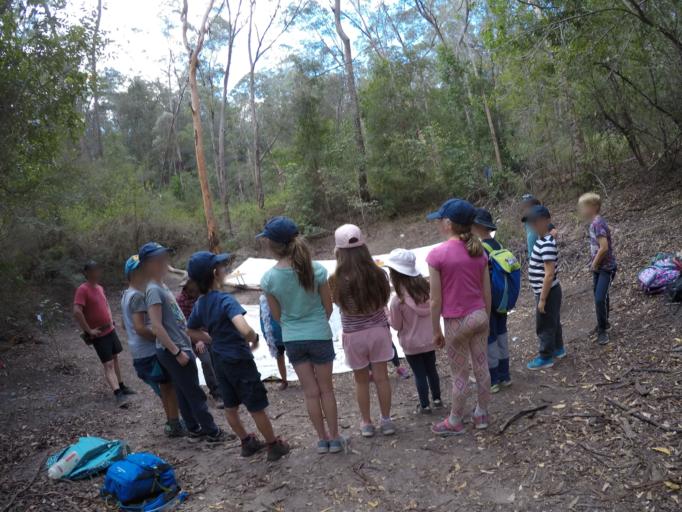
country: AU
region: New South Wales
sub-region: Hawkesbury
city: Pitt Town
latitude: -33.4690
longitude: 150.8913
